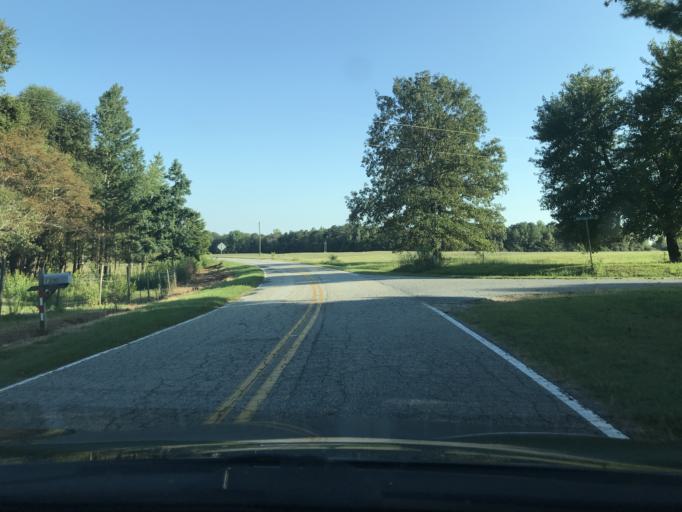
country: US
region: South Carolina
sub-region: Spartanburg County
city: Mayo
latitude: 35.1101
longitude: -81.7846
